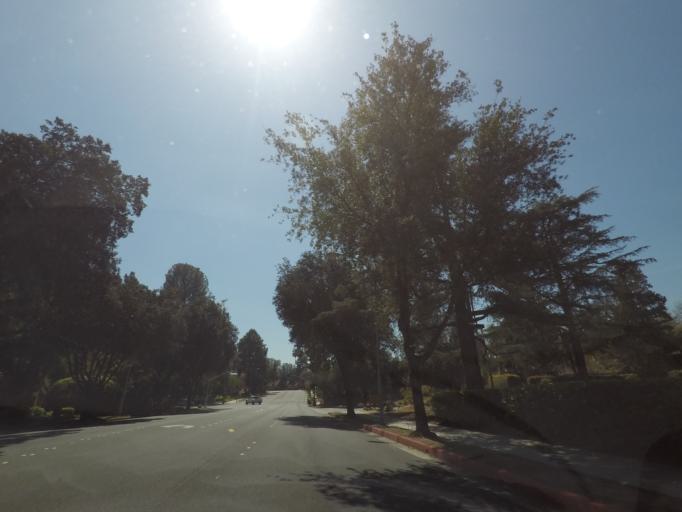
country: US
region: California
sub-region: Los Angeles County
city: Pasadena
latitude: 34.1505
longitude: -118.1608
